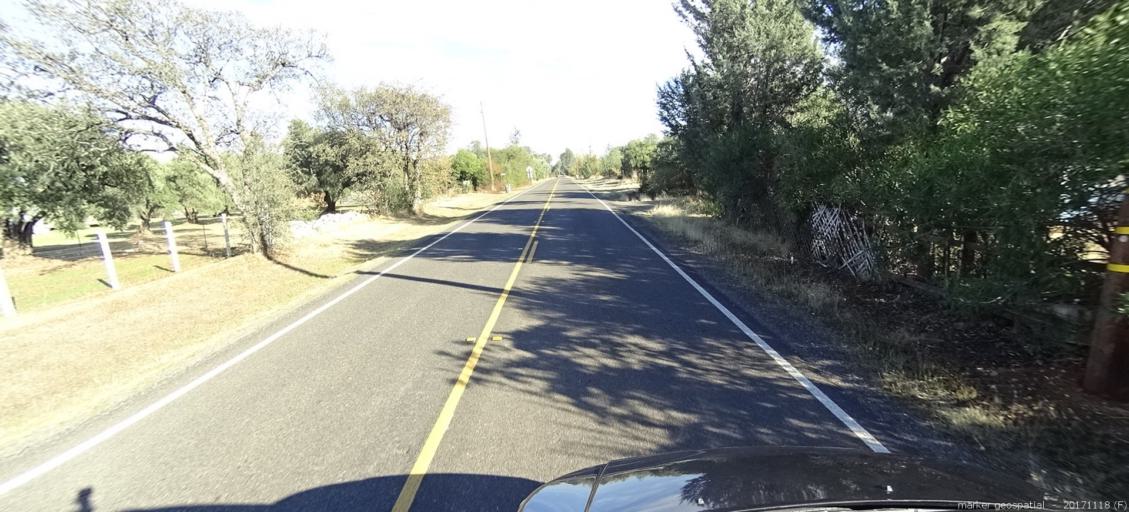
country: US
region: California
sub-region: Shasta County
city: Anderson
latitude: 40.4456
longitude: -122.4349
